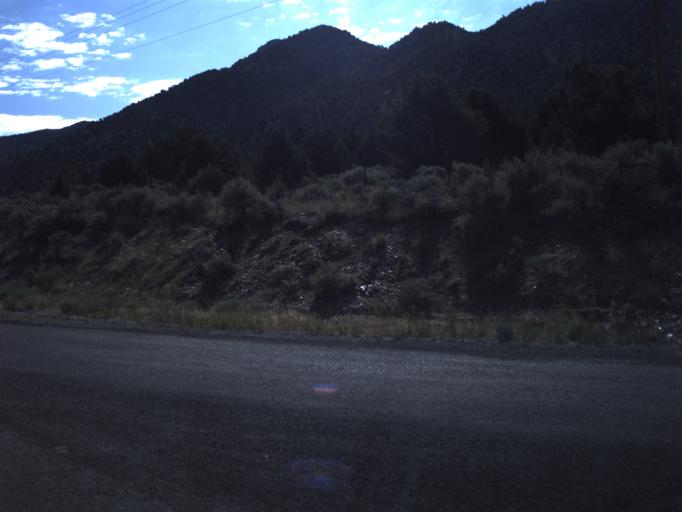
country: US
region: Utah
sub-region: Utah County
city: Genola
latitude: 39.9434
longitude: -112.1433
